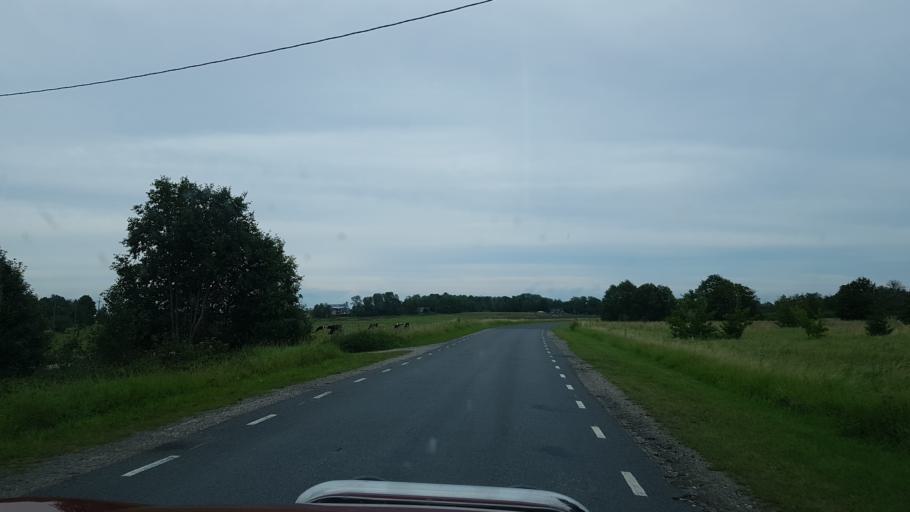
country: EE
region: Laeaene
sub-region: Lihula vald
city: Lihula
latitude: 58.8823
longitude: 23.8314
